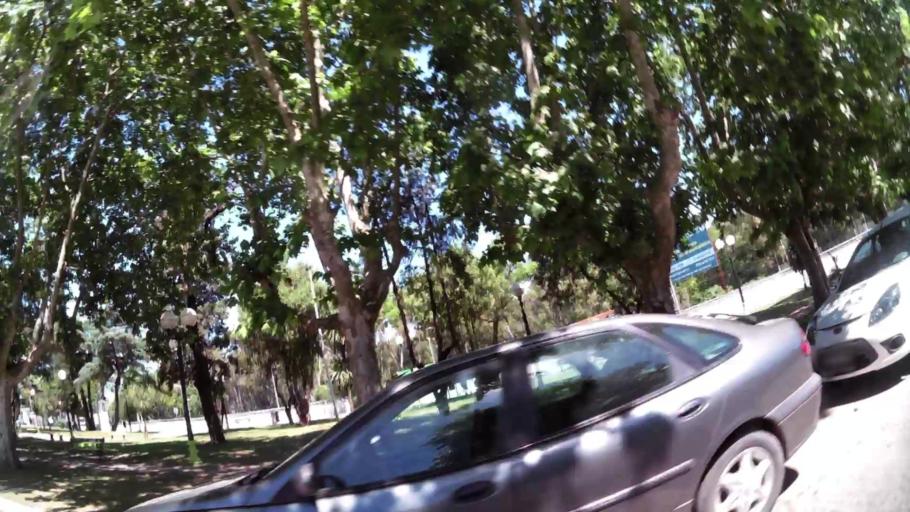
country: AR
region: Buenos Aires
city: Hurlingham
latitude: -34.5019
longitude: -58.6473
